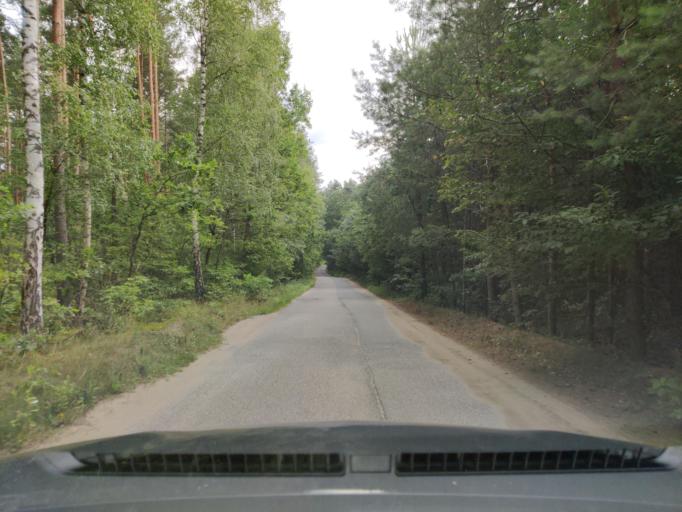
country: PL
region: Masovian Voivodeship
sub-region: Powiat pultuski
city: Pultusk
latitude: 52.7376
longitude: 21.1385
